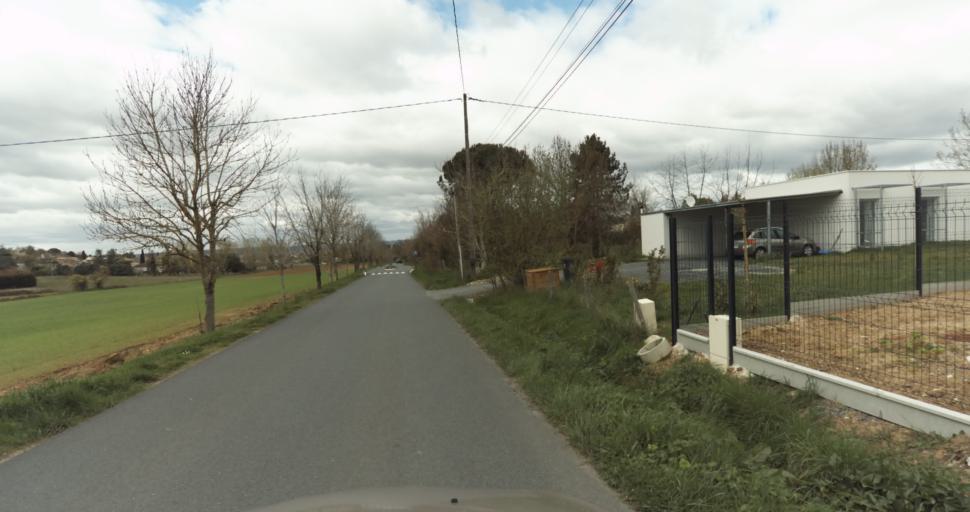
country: FR
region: Midi-Pyrenees
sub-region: Departement du Tarn
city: Puygouzon
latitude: 43.9077
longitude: 2.1727
